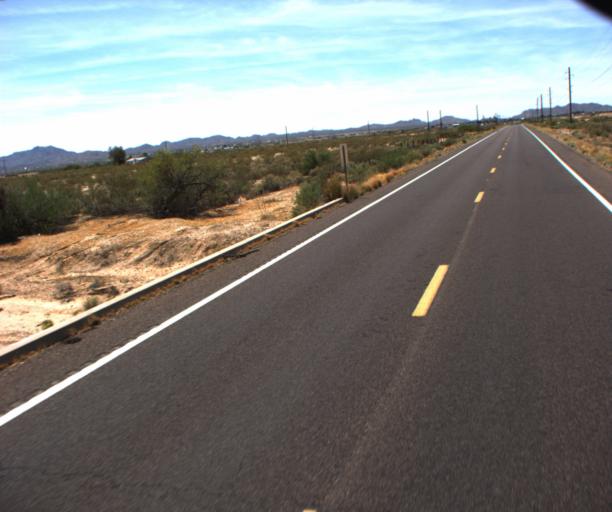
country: US
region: Arizona
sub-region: La Paz County
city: Salome
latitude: 33.7960
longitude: -113.5889
